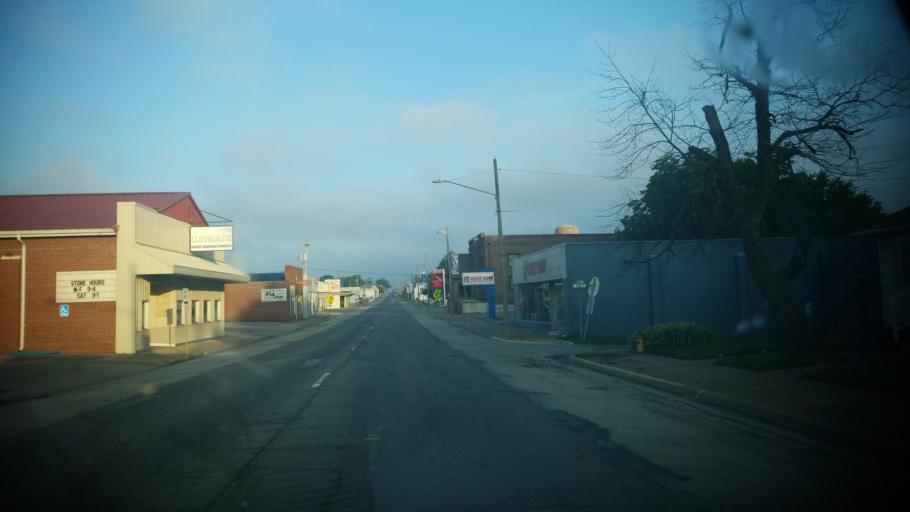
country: US
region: Illinois
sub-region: Wayne County
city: Fairfield
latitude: 38.3797
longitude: -88.3614
